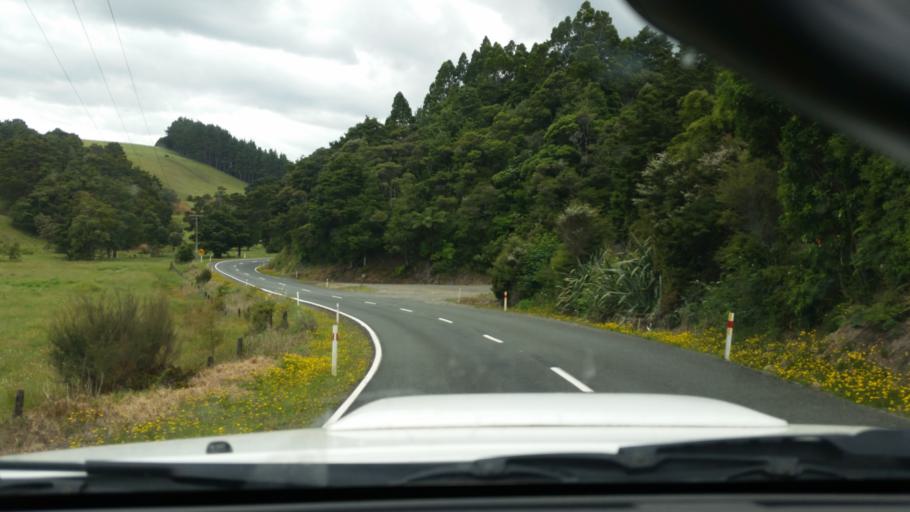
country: NZ
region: Northland
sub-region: Kaipara District
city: Dargaville
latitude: -35.8125
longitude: 173.7275
